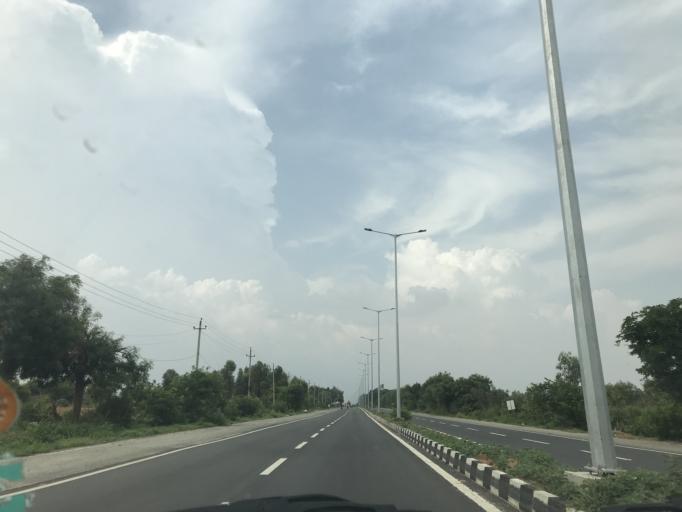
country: IN
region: Karnataka
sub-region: Bangalore Rural
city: Devanhalli
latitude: 13.1577
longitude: 77.6822
